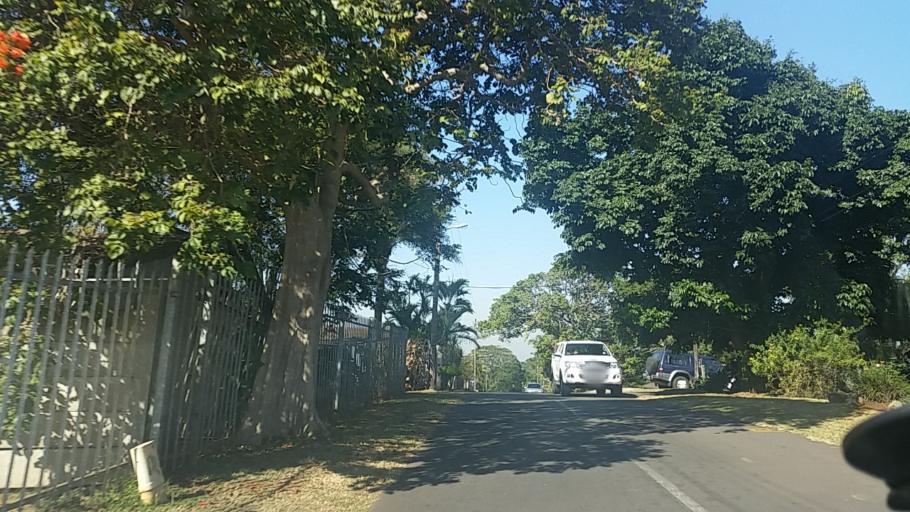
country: ZA
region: KwaZulu-Natal
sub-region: eThekwini Metropolitan Municipality
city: Berea
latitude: -29.8527
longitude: 30.9013
